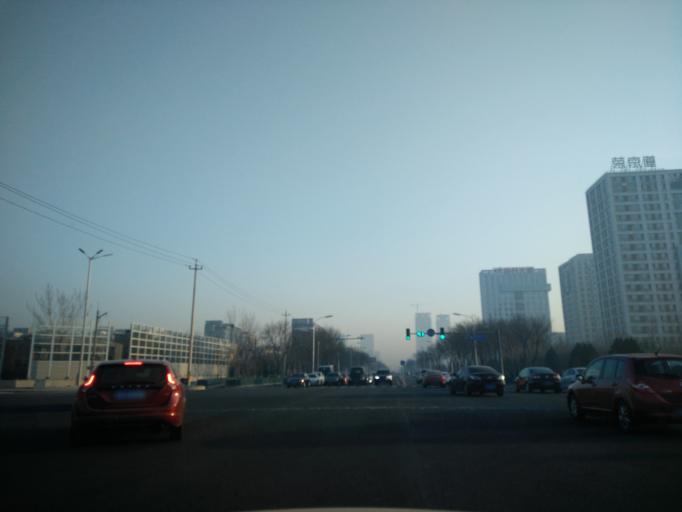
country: CN
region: Beijing
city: Jiugong
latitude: 39.7832
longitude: 116.4865
